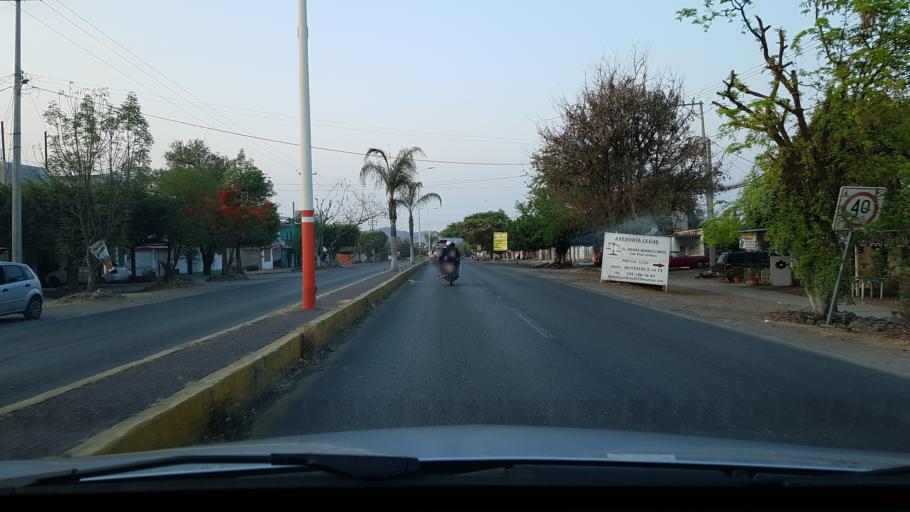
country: MX
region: Morelos
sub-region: Jonacatepec
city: Amacuitlapilco
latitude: 18.6940
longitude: -98.8017
